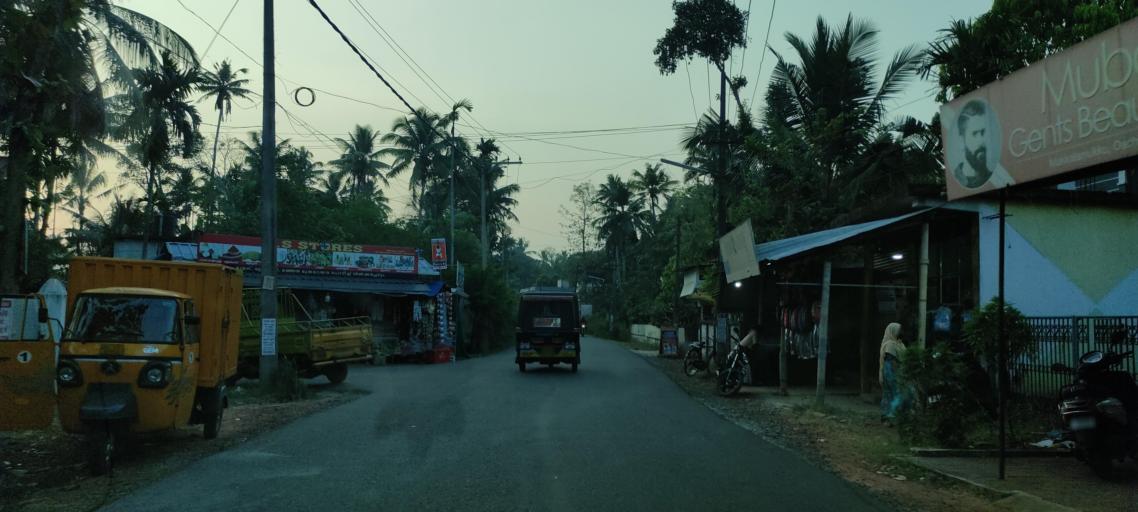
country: IN
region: Kerala
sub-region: Alappuzha
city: Kayankulam
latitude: 9.1376
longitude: 76.5163
